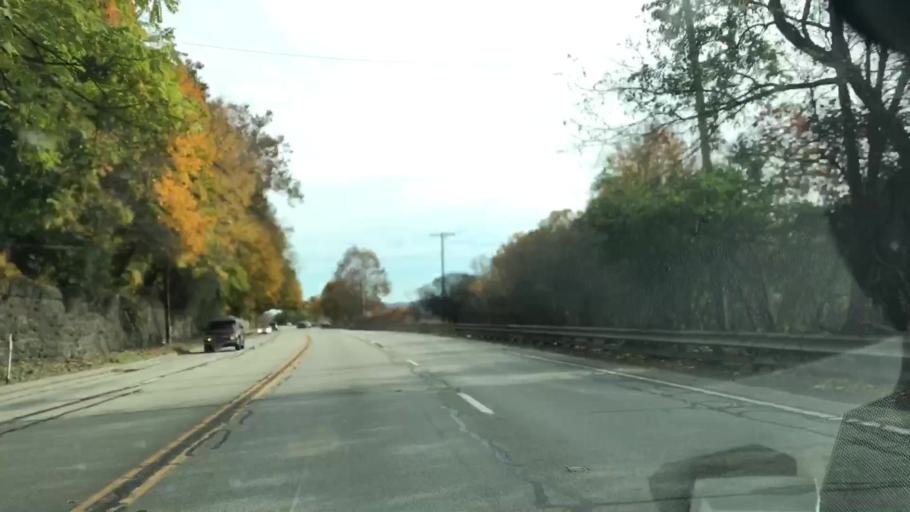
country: US
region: Pennsylvania
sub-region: Allegheny County
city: Coraopolis
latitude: 40.5306
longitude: -80.1722
